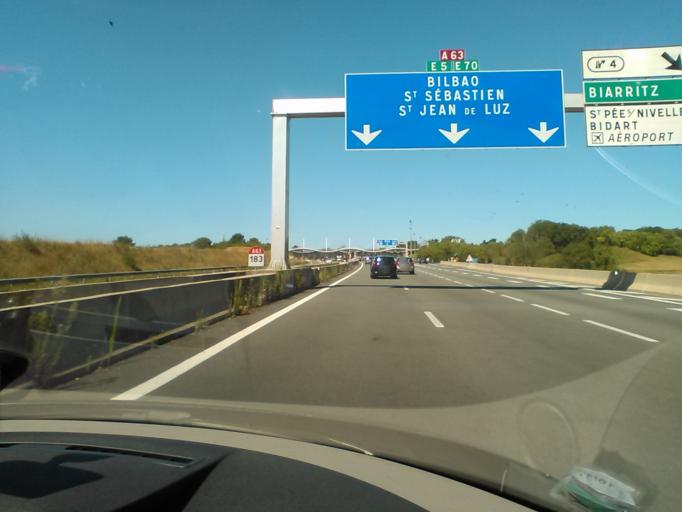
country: FR
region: Aquitaine
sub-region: Departement des Pyrenees-Atlantiques
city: Arbonne
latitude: 43.4478
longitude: -1.5476
